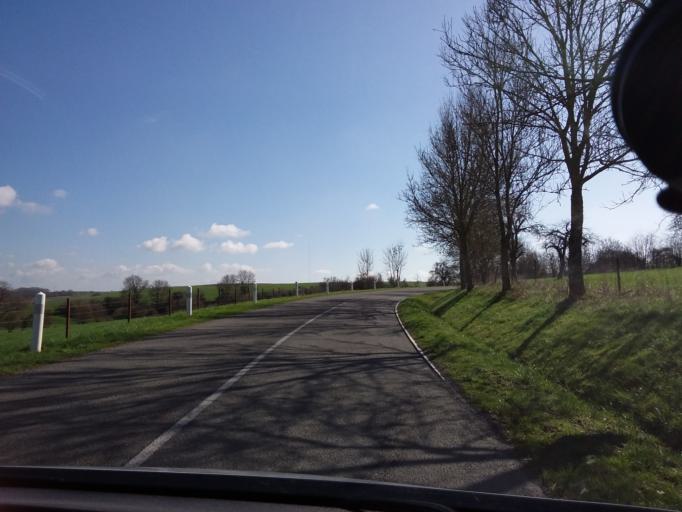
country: FR
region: Picardie
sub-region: Departement de l'Aisne
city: Montcornet
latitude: 49.7374
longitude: 3.9958
